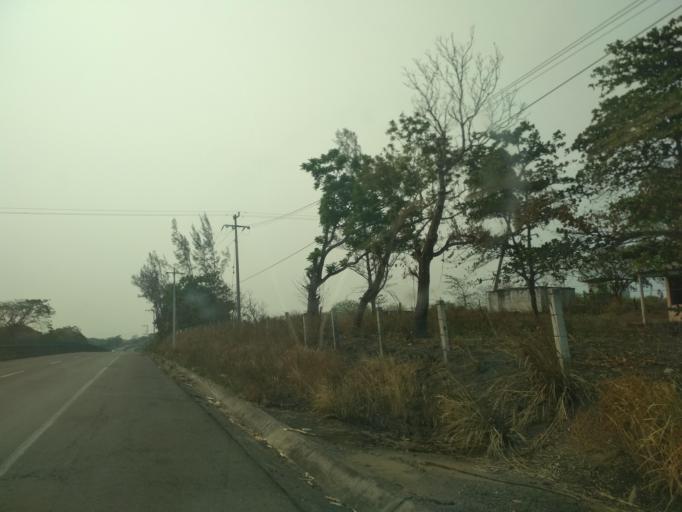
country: MX
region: Veracruz
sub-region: Veracruz
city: Las Amapolas
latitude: 19.1451
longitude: -96.2436
